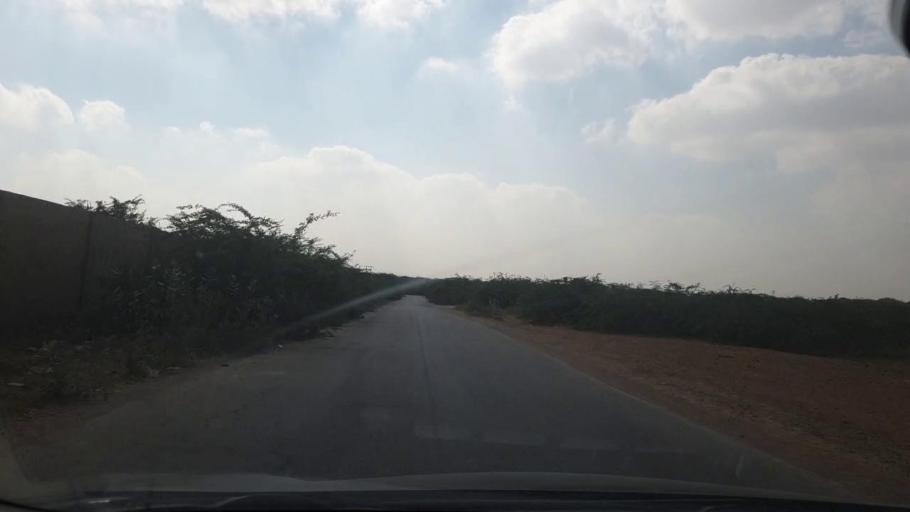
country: PK
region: Sindh
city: Malir Cantonment
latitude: 25.0163
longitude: 67.3531
